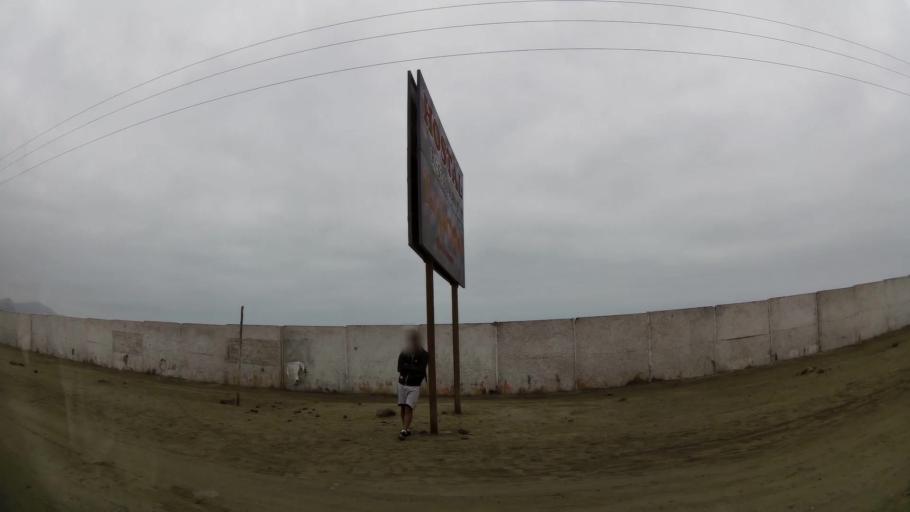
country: PE
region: Lima
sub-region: Lima
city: Punta Hermosa
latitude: -12.3538
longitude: -76.8073
